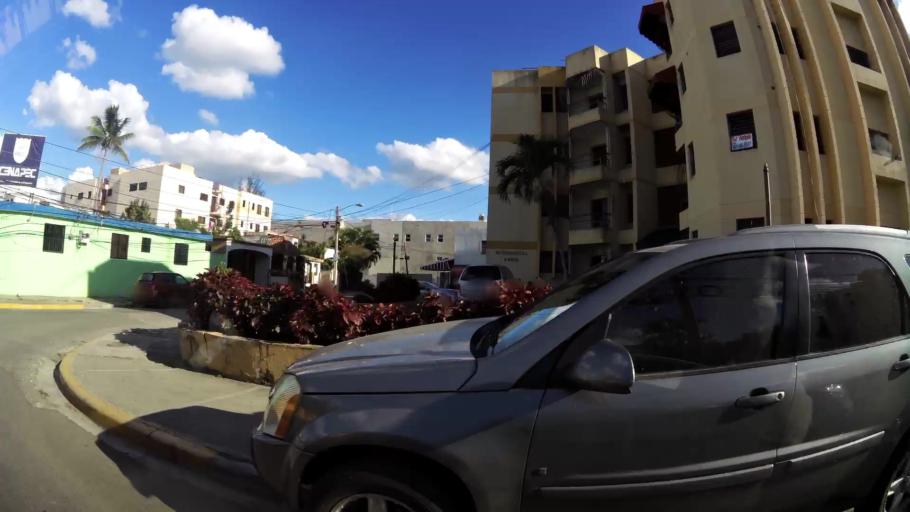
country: DO
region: Santiago
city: Santiago de los Caballeros
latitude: 19.4591
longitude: -70.6977
